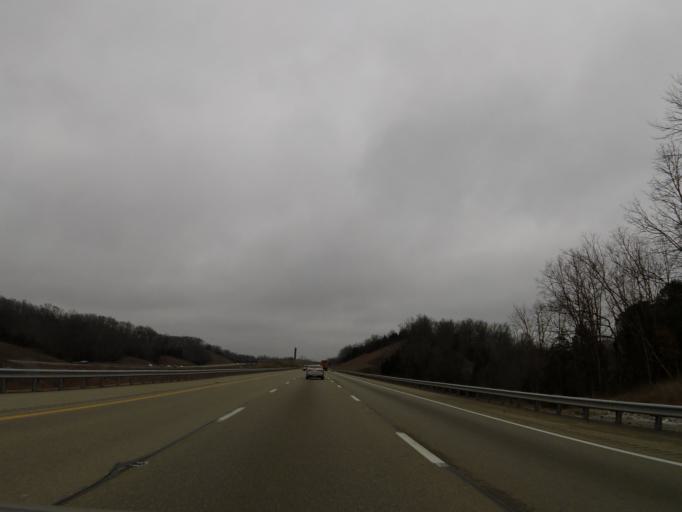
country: US
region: Kentucky
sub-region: Grant County
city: Williamstown
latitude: 38.5365
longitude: -84.5917
